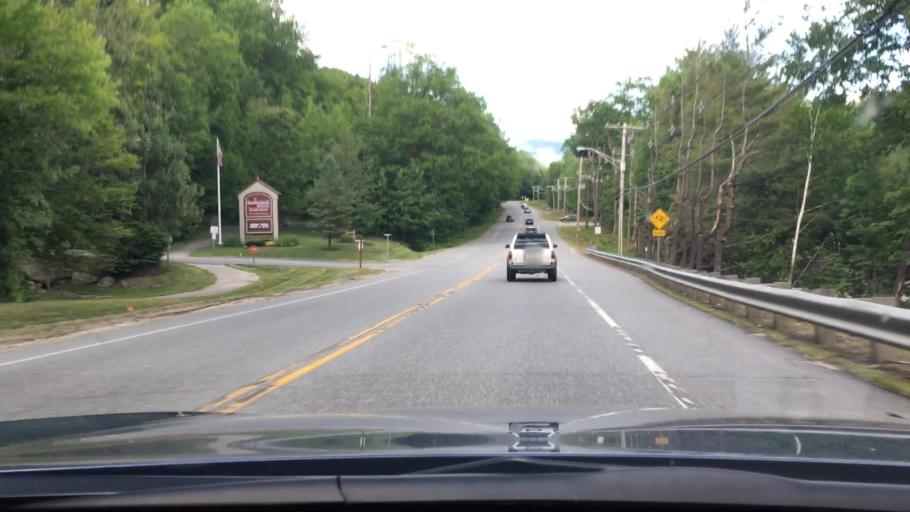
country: US
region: New Hampshire
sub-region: Grafton County
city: Woodstock
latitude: 44.0529
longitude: -71.6513
